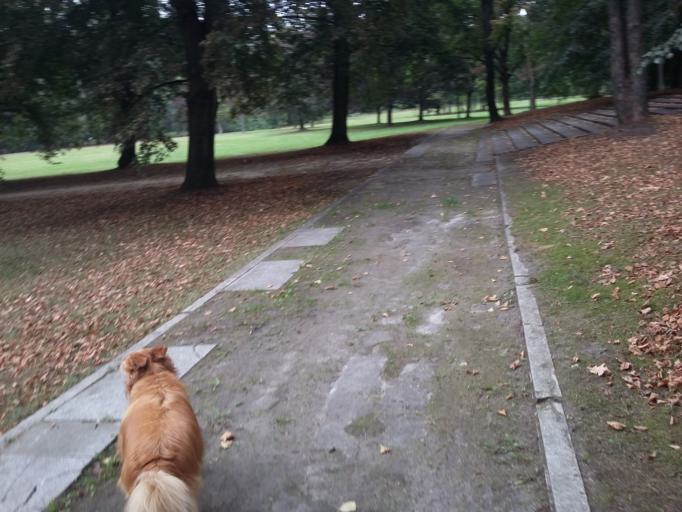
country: PL
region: Lodz Voivodeship
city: Lodz
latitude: 51.7667
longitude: 19.4146
